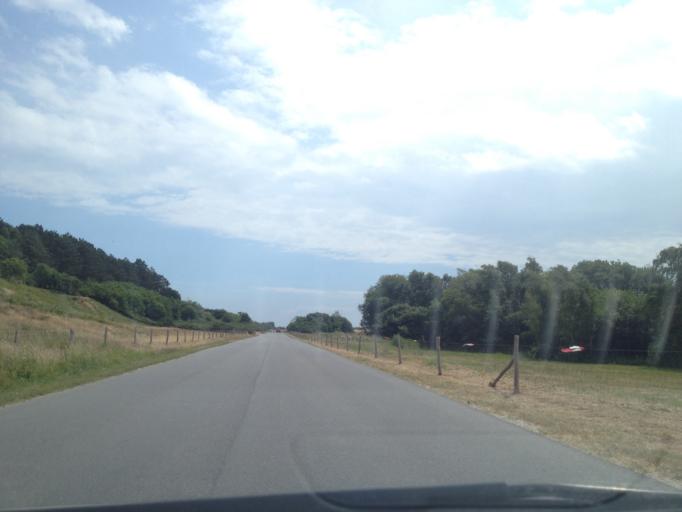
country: DK
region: Central Jutland
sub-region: Syddjurs Kommune
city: Ebeltoft
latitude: 56.1555
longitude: 10.6796
